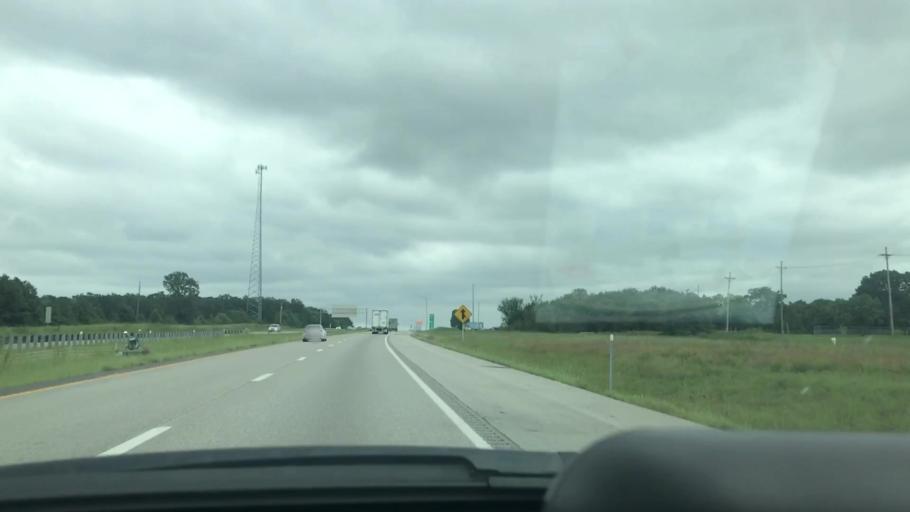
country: US
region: Kansas
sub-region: Cherokee County
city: Galena
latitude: 36.9990
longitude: -94.6087
